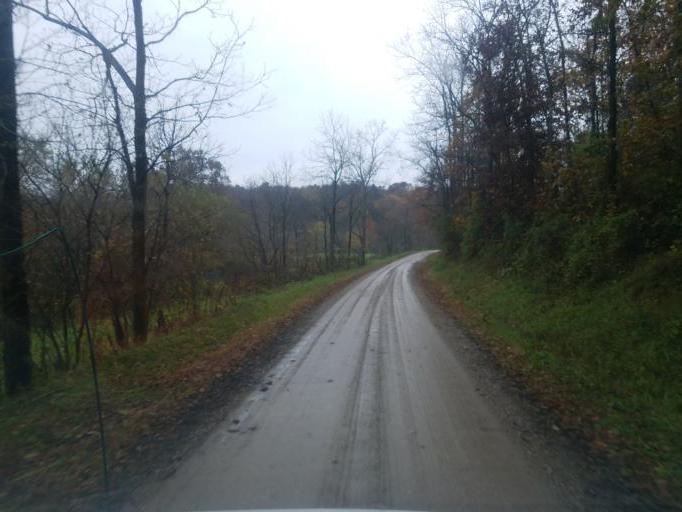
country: US
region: Ohio
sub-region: Washington County
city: Beverly
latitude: 39.4590
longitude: -81.7691
